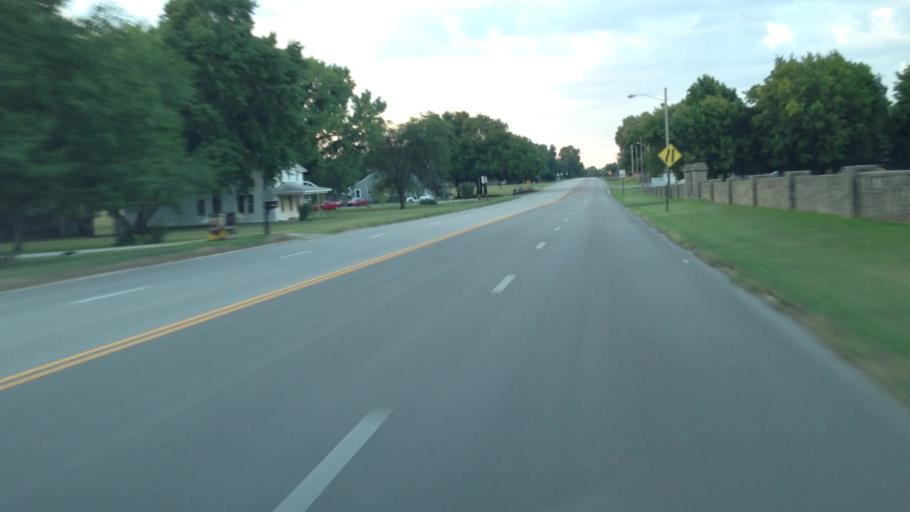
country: US
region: Kansas
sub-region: Montgomery County
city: Independence
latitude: 37.2482
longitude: -95.7063
